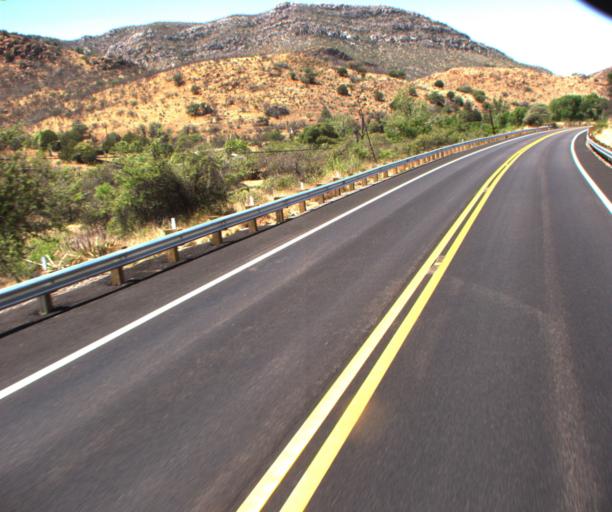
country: US
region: Arizona
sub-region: Cochise County
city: Bisbee
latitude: 31.4984
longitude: -110.0010
